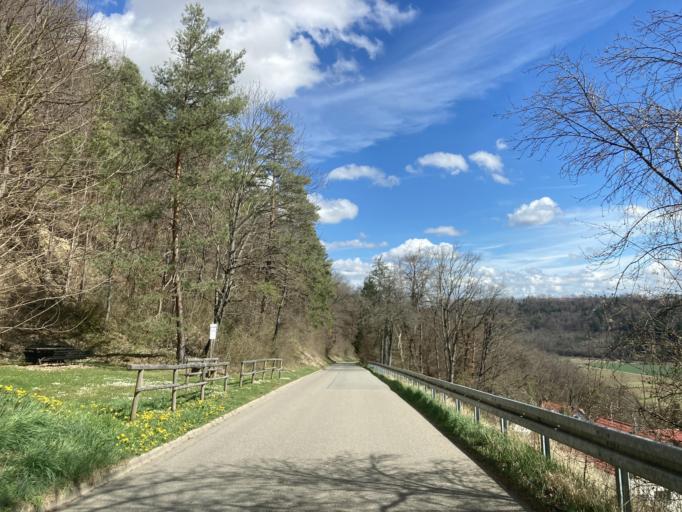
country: DE
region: Baden-Wuerttemberg
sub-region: Tuebingen Region
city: Hirrlingen
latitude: 48.4543
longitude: 8.8572
